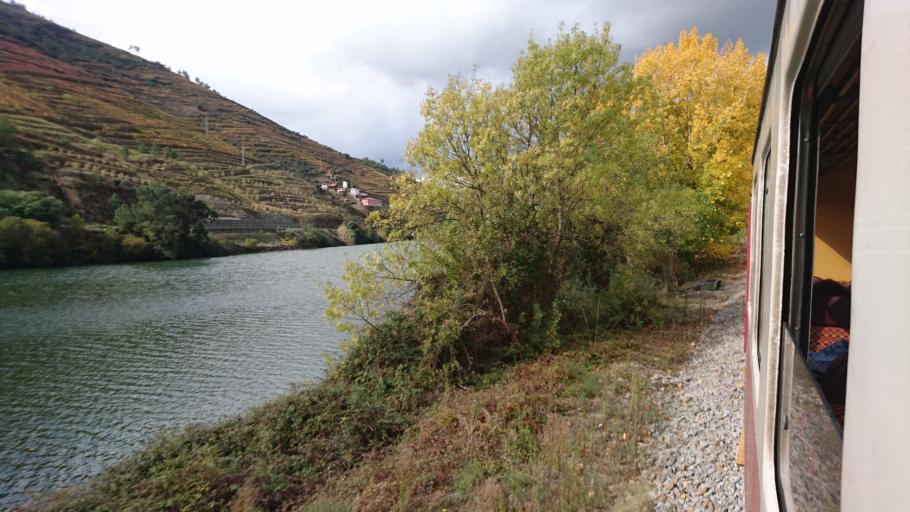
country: PT
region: Viseu
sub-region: Armamar
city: Armamar
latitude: 41.1437
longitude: -7.7037
